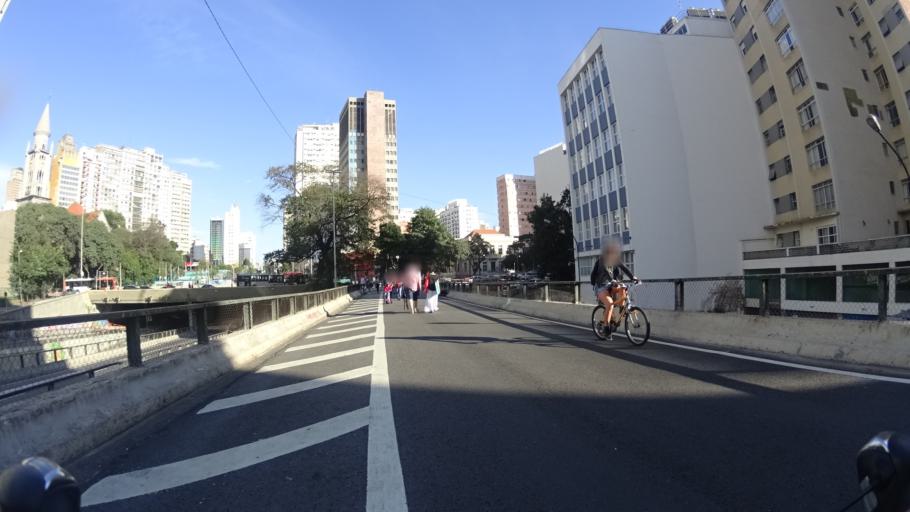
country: BR
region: Sao Paulo
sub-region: Sao Paulo
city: Sao Paulo
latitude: -23.5467
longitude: -46.6479
